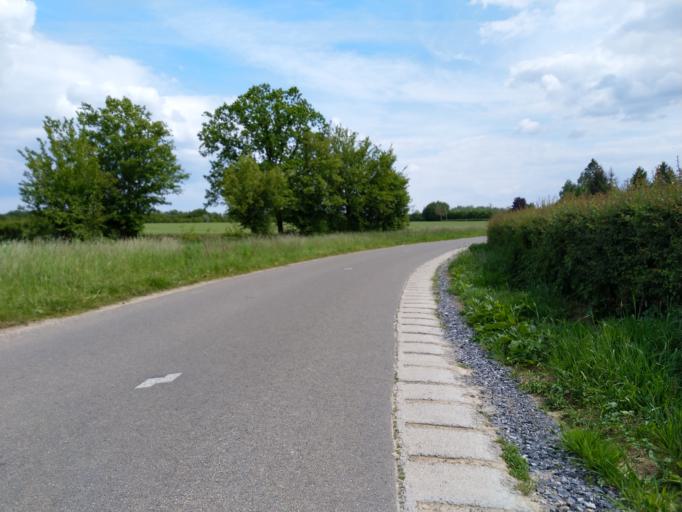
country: FR
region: Picardie
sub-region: Departement de l'Aisne
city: Boue
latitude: 50.0239
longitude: 3.6868
